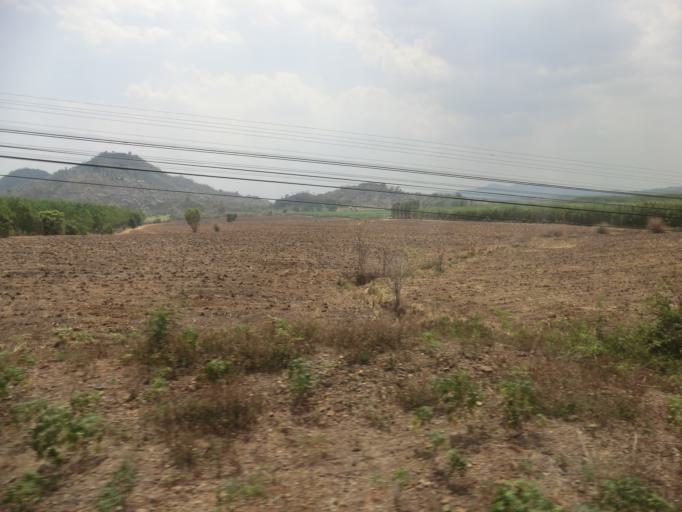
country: VN
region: Binh Thuan
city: Thuan Nam
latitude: 10.8875
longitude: 107.7036
